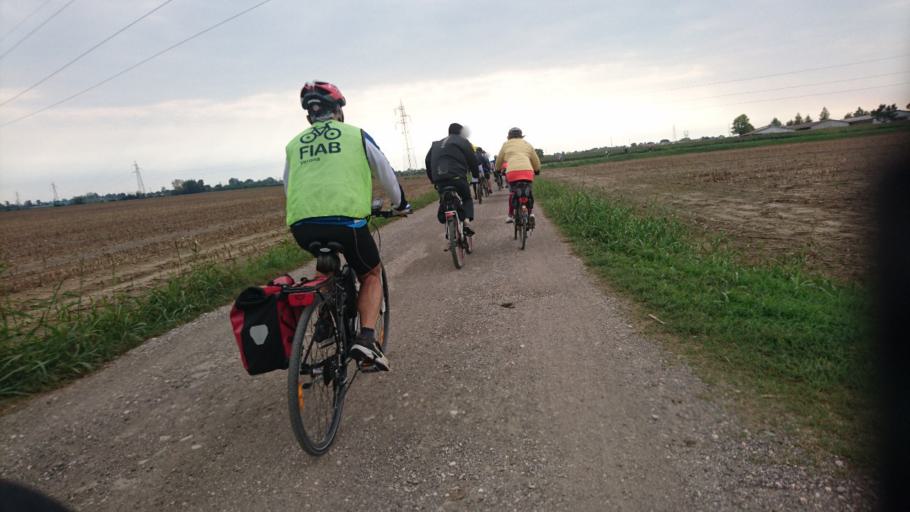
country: IT
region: Veneto
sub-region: Provincia di Verona
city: San Martino Buon Albergo
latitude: 45.4015
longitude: 11.1127
